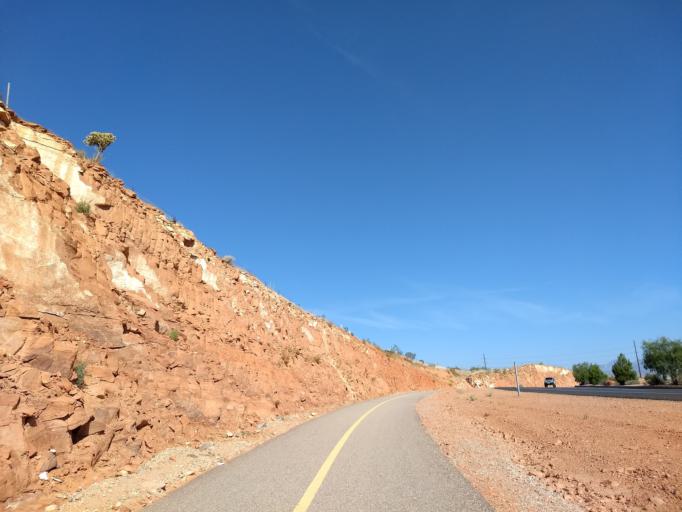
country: US
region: Utah
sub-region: Washington County
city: Saint George
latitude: 37.1228
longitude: -113.5844
